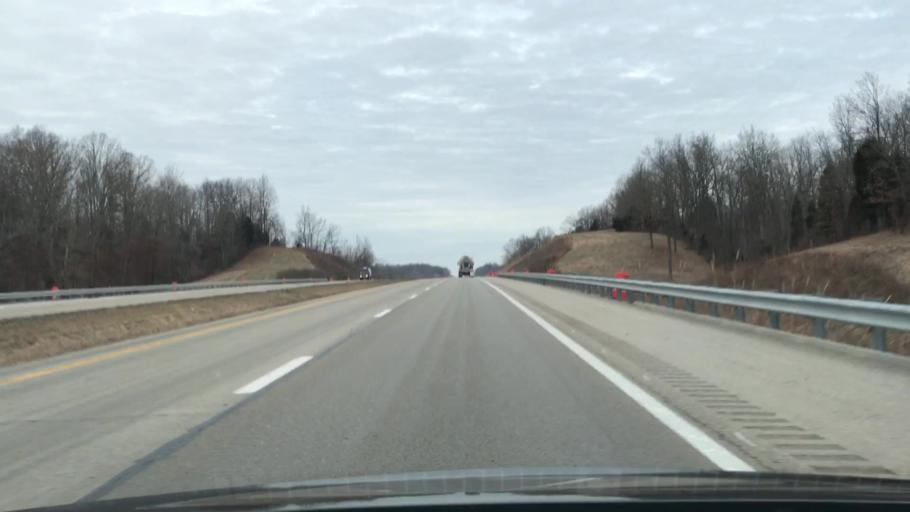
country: US
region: Kentucky
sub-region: Ohio County
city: Hartford
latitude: 37.5661
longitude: -86.9467
